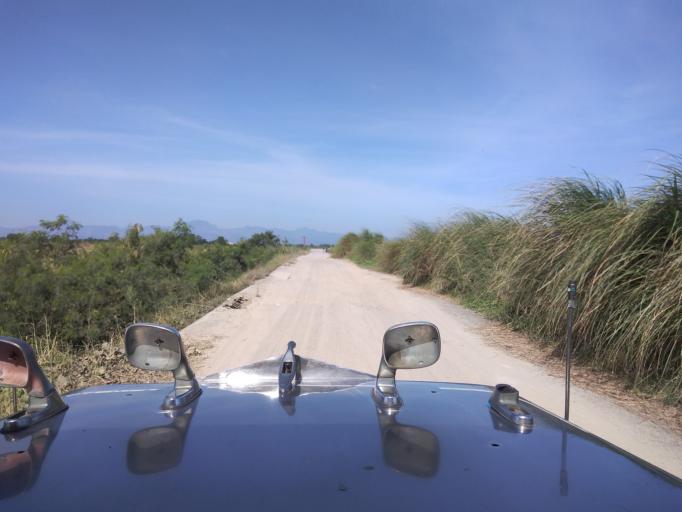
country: PH
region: Central Luzon
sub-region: Province of Pampanga
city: Bacolor
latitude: 14.9929
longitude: 120.6714
